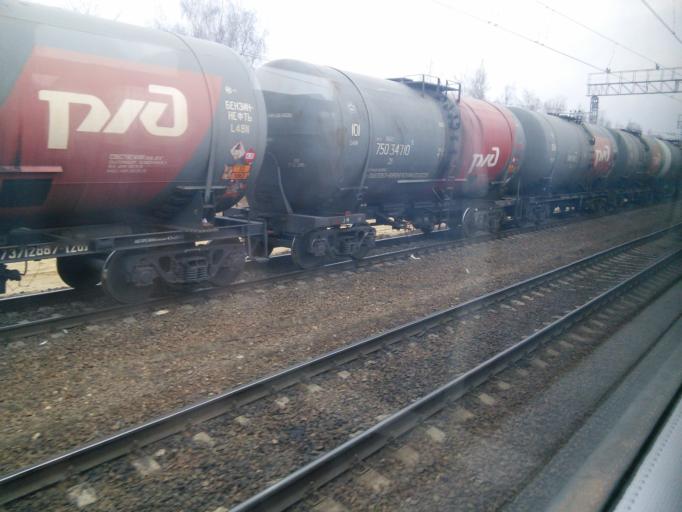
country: RU
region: Moskovskaya
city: Yakovlevskoye
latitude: 55.4279
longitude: 37.8822
